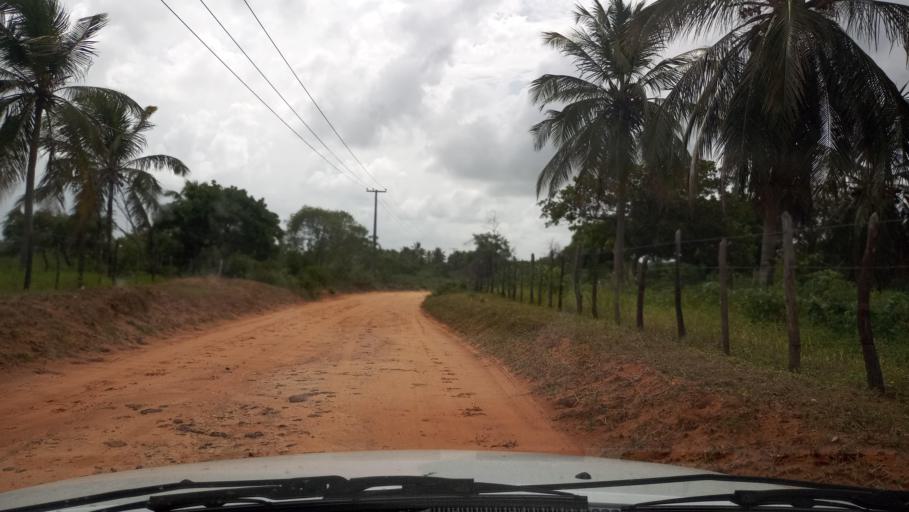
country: BR
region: Rio Grande do Norte
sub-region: Maxaranguape
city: Sao Miguel
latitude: -5.4837
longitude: -35.3144
